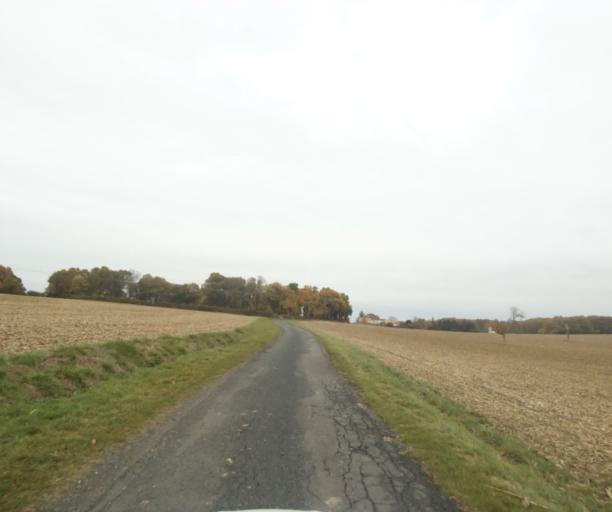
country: FR
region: Poitou-Charentes
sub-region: Departement de la Charente-Maritime
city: Saint-Georges-des-Coteaux
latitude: 45.7372
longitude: -0.6874
